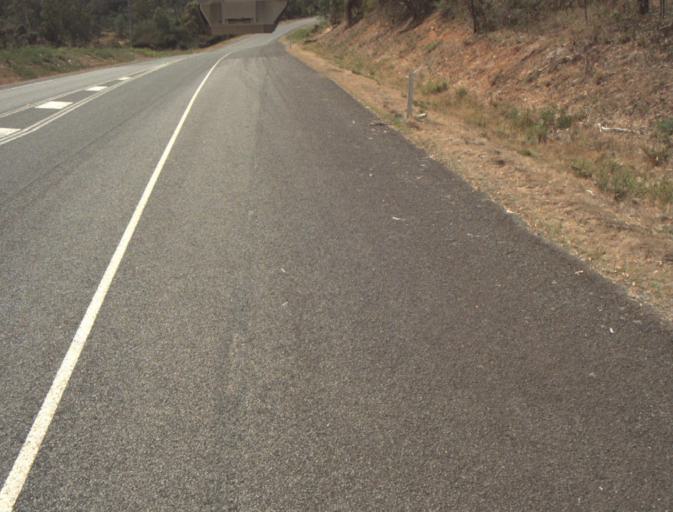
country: AU
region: Tasmania
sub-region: Launceston
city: Mayfield
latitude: -41.3057
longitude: 147.0487
